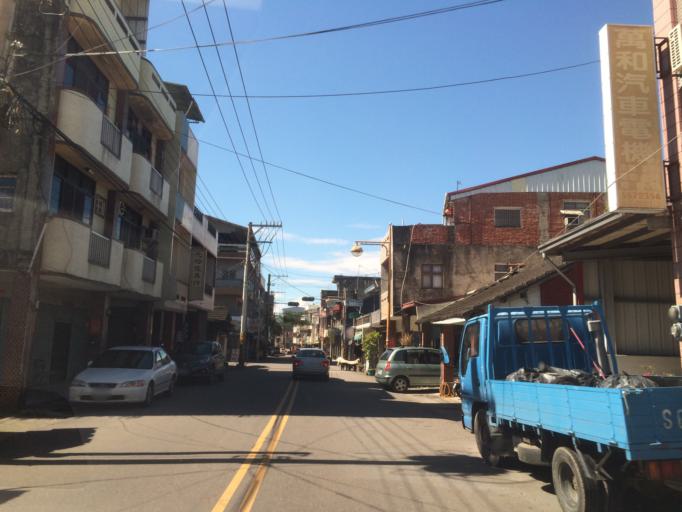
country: TW
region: Taiwan
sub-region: Yunlin
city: Douliu
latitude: 23.7023
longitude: 120.6014
